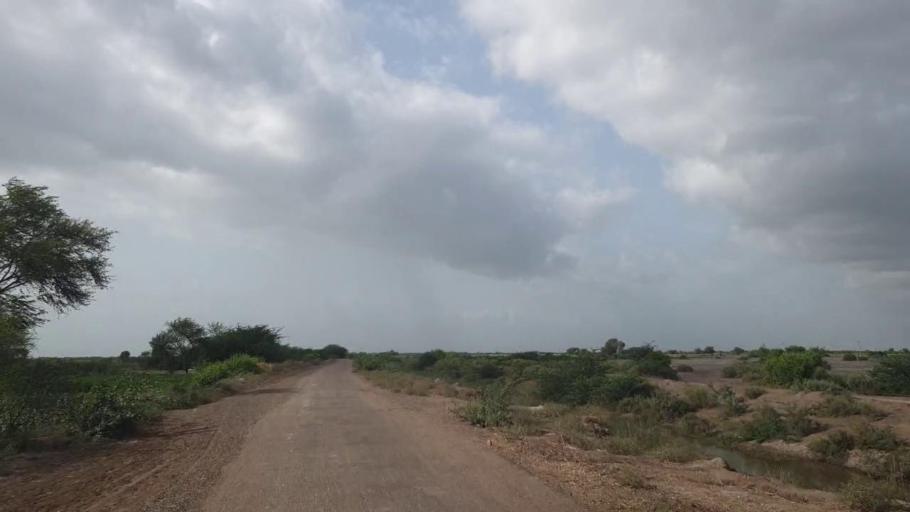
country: PK
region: Sindh
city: Kadhan
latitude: 24.5589
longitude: 69.0638
